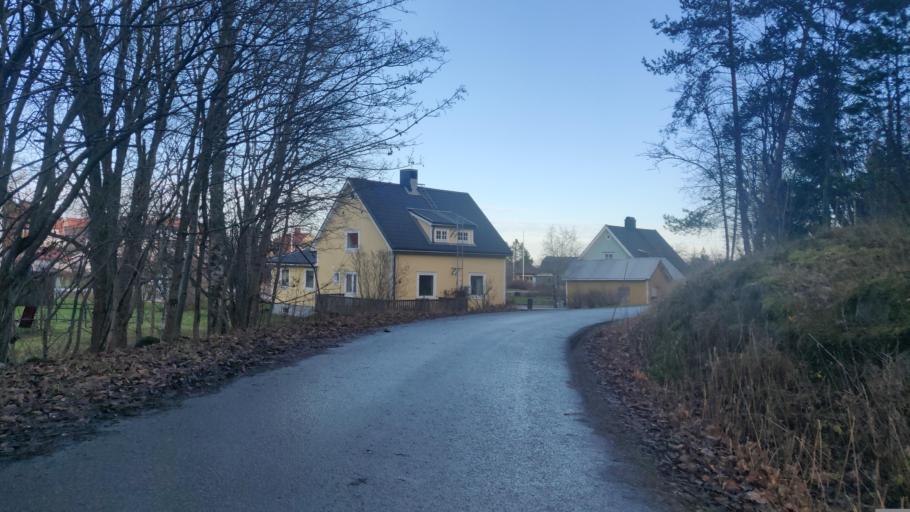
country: SE
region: Vaesternorrland
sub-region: Sundsvalls Kommun
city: Kvissleby
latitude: 62.3099
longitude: 17.3660
